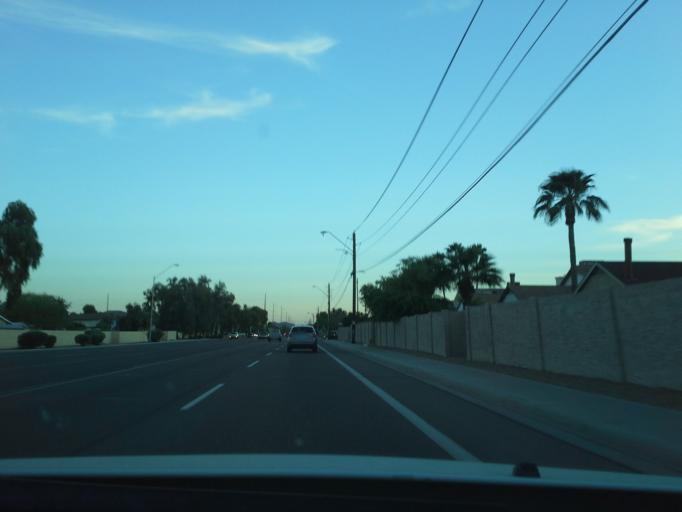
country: US
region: Arizona
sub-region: Maricopa County
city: Glendale
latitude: 33.6599
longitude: -112.0657
